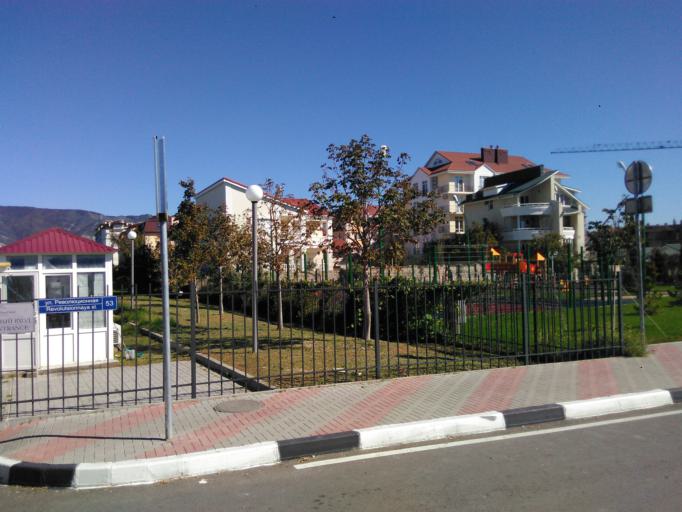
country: RU
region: Krasnodarskiy
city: Gelendzhik
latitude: 44.5494
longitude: 38.0539
